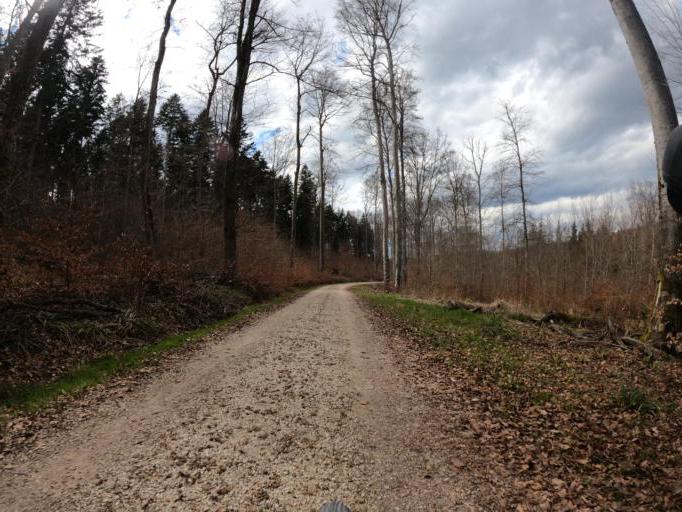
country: DE
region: Baden-Wuerttemberg
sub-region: Tuebingen Region
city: Gomaringen
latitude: 48.4335
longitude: 9.1167
